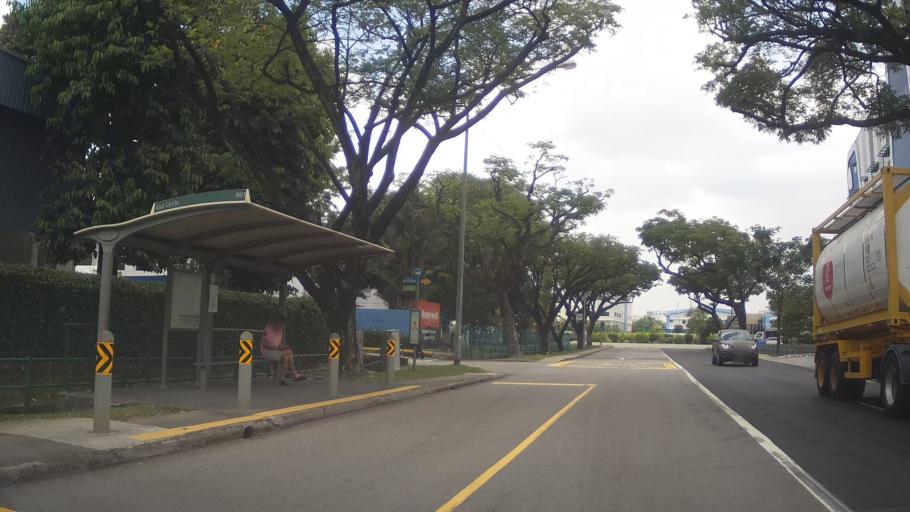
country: MY
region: Johor
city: Johor Bahru
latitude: 1.3205
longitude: 103.6778
